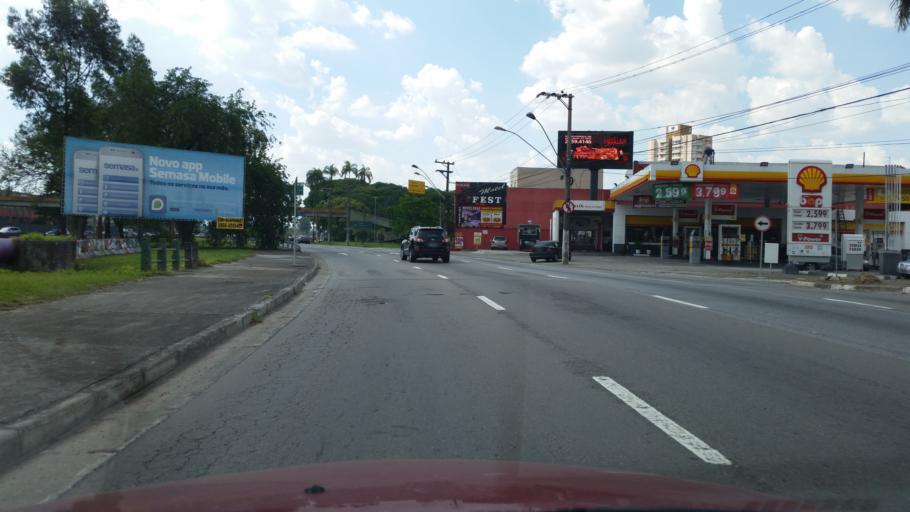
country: BR
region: Sao Paulo
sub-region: Sao Caetano Do Sul
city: Sao Caetano do Sul
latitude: -23.6383
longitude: -46.5342
